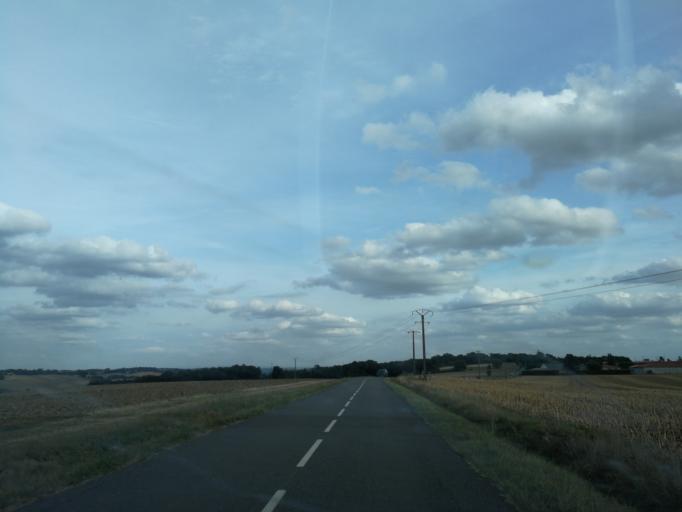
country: FR
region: Midi-Pyrenees
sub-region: Departement de la Haute-Garonne
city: Flourens
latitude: 43.6082
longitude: 1.5399
